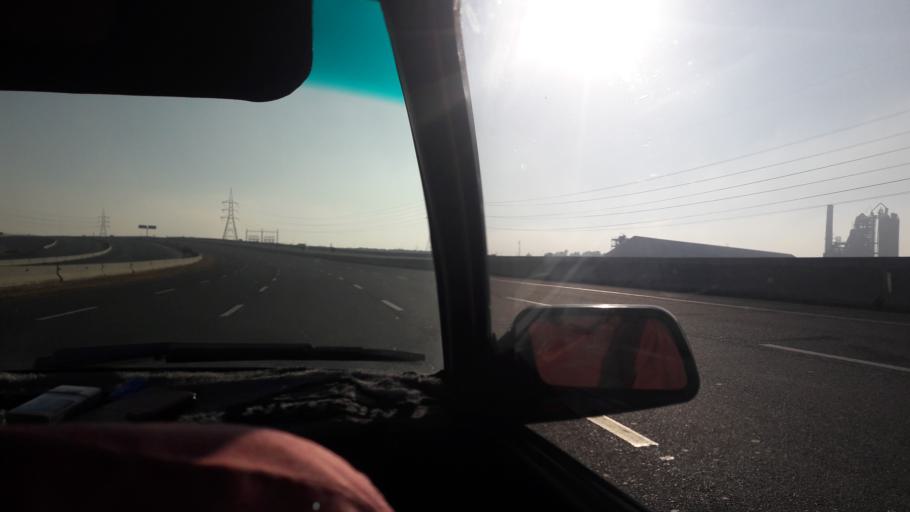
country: EG
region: Muhafazat al Qahirah
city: Halwan
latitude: 29.9204
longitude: 31.5202
